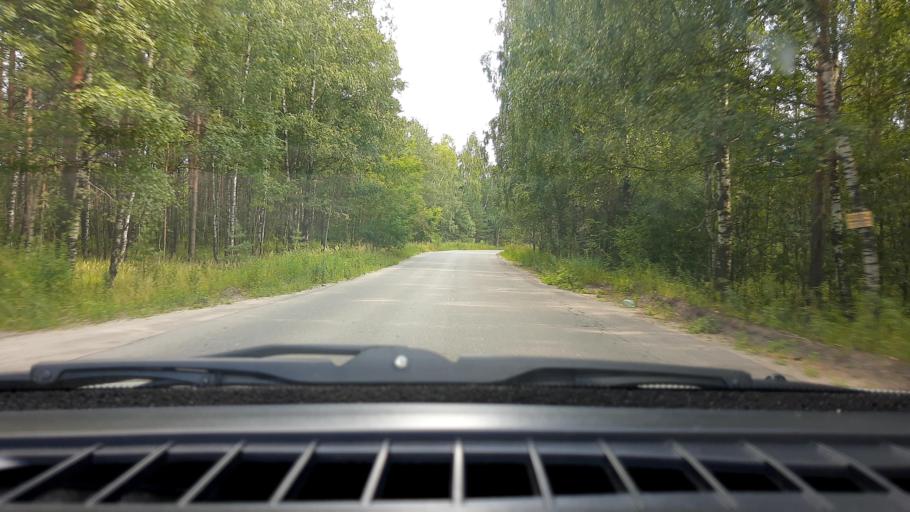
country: RU
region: Nizjnij Novgorod
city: Babino
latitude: 56.3132
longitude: 43.6279
